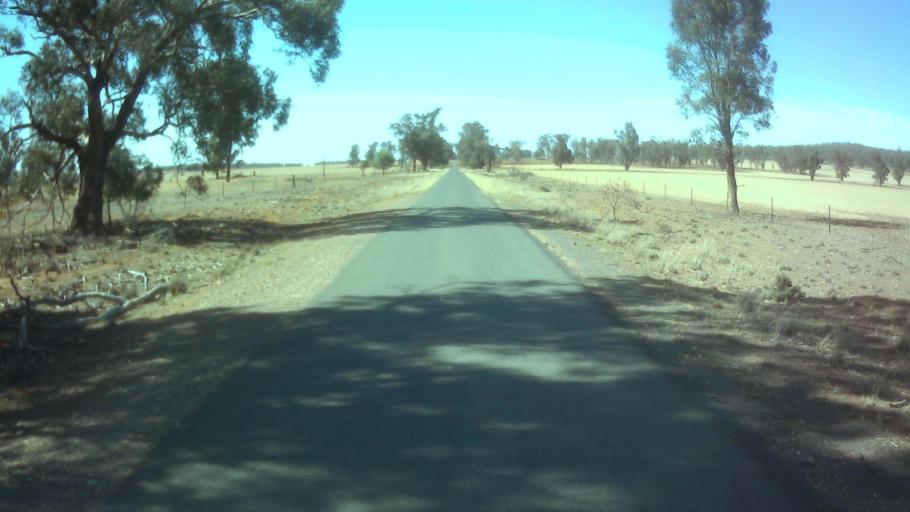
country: AU
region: New South Wales
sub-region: Forbes
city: Forbes
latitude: -33.7370
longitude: 147.7416
